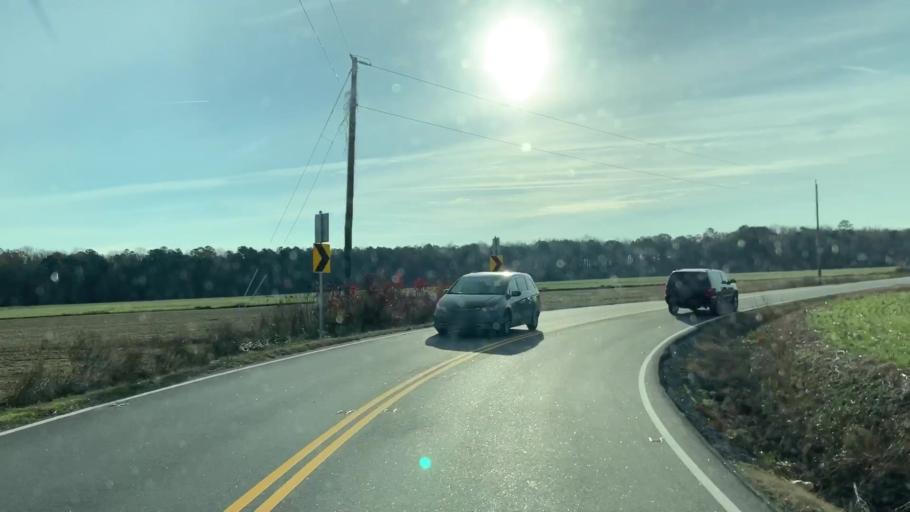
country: US
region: Virginia
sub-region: City of Virginia Beach
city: Virginia Beach
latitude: 36.7171
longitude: -76.0503
